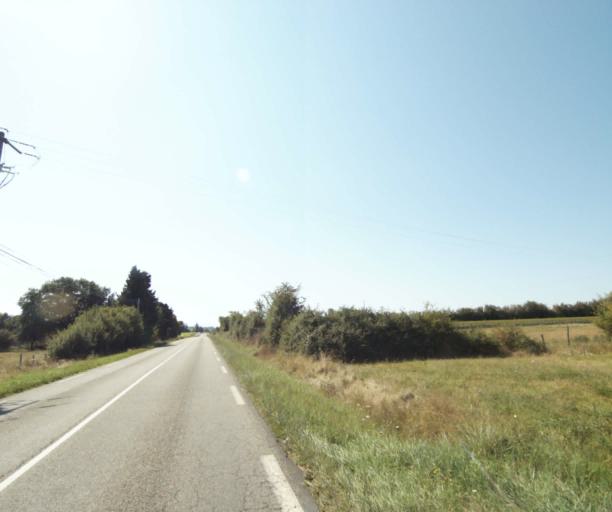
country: FR
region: Midi-Pyrenees
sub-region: Departement de l'Ariege
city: Lezat-sur-Leze
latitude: 43.2968
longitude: 1.3385
